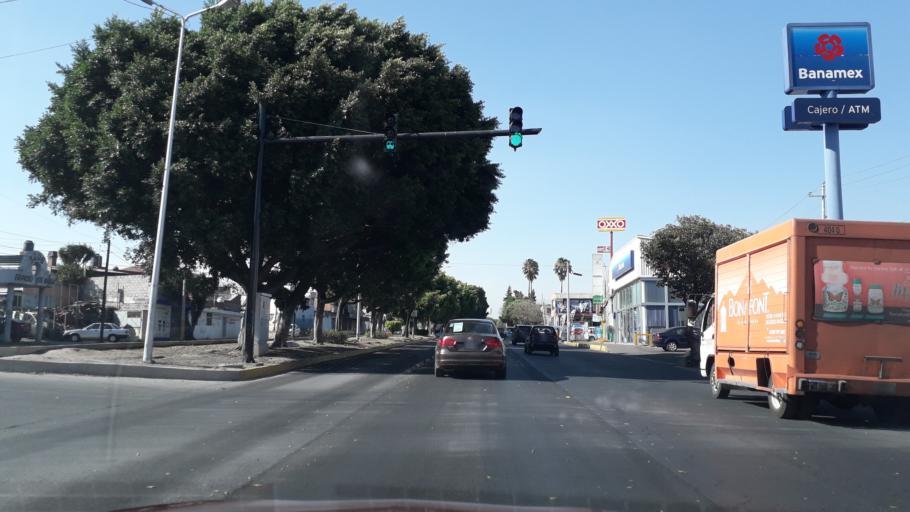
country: MX
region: Puebla
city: Puebla
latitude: 19.0573
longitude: -98.1927
